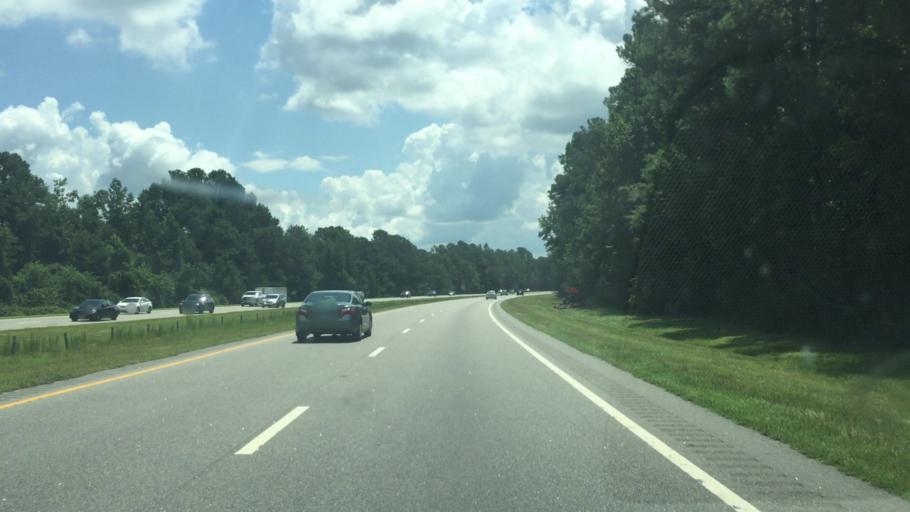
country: US
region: North Carolina
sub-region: Robeson County
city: Lumberton
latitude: 34.5716
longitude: -79.0339
